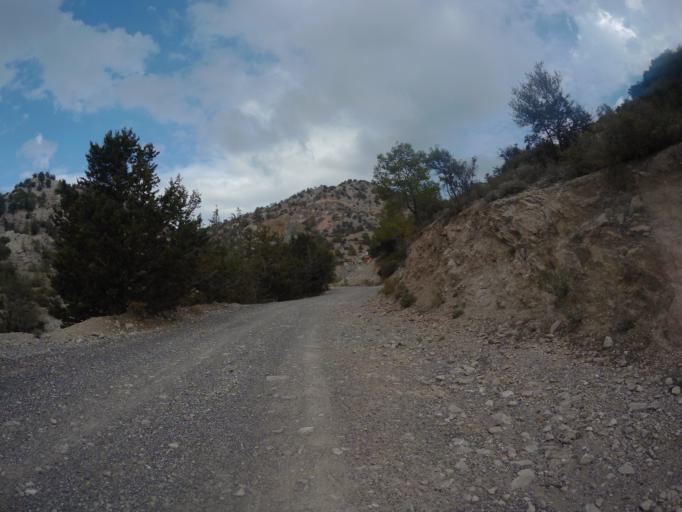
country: CY
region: Ammochostos
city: Lefkonoiko
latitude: 35.3445
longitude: 33.7248
